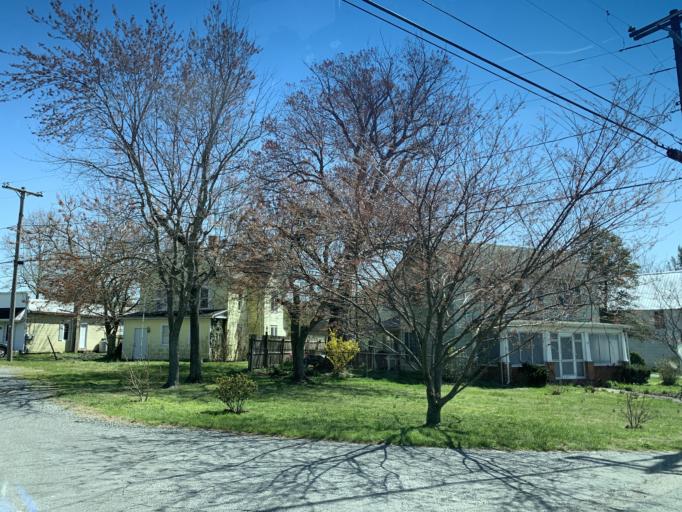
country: US
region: Maryland
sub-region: Talbot County
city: Easton
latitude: 38.8754
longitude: -75.9957
